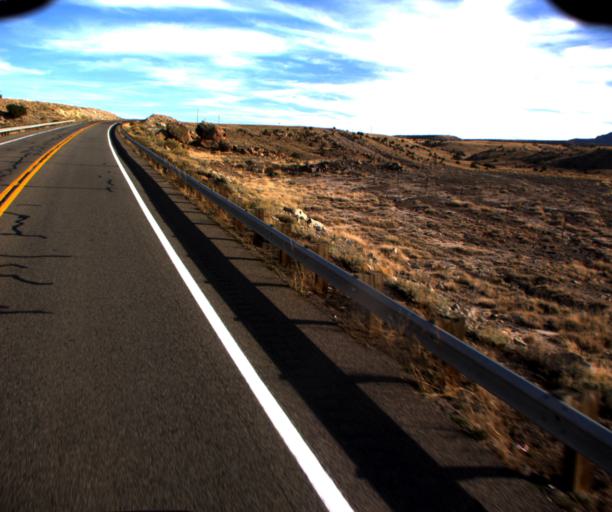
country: US
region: New Mexico
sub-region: San Juan County
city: Shiprock
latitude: 36.9151
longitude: -109.0773
